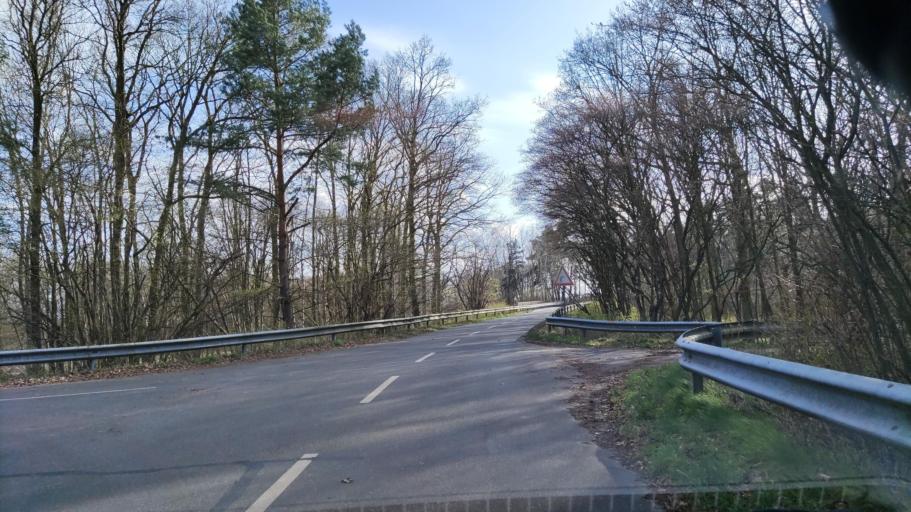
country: DE
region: Lower Saxony
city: Jelmstorf
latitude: 53.1251
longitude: 10.5200
